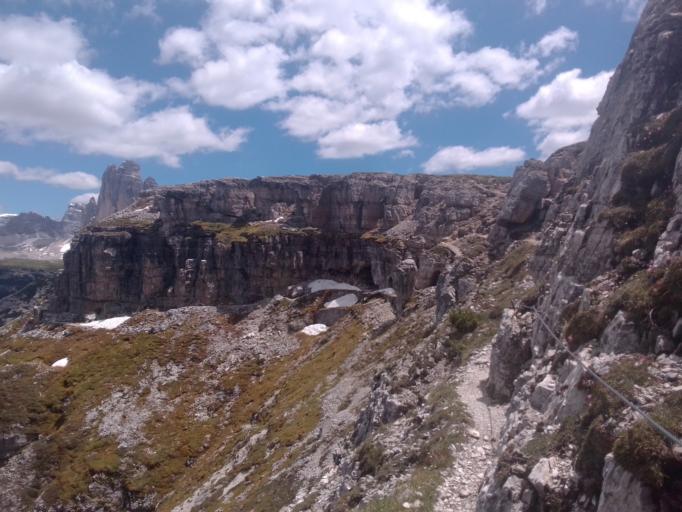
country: IT
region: Trentino-Alto Adige
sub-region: Bolzano
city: Dobbiaco
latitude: 46.6241
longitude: 12.2453
